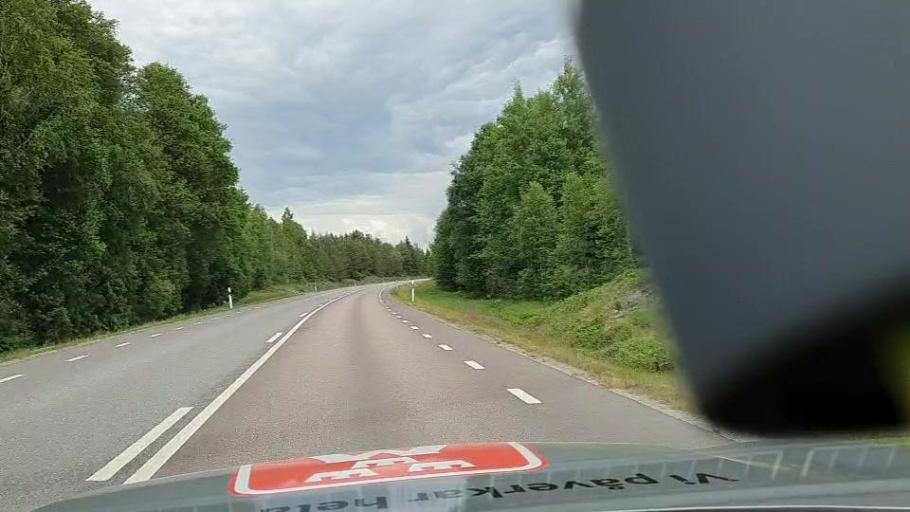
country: SE
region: Kalmar
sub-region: Emmaboda Kommun
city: Emmaboda
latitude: 56.4495
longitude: 15.5648
